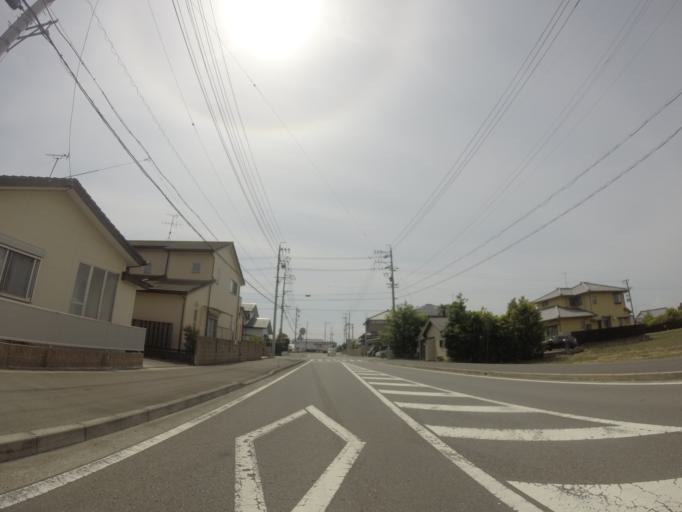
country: JP
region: Shizuoka
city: Fujieda
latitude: 34.8071
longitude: 138.2885
